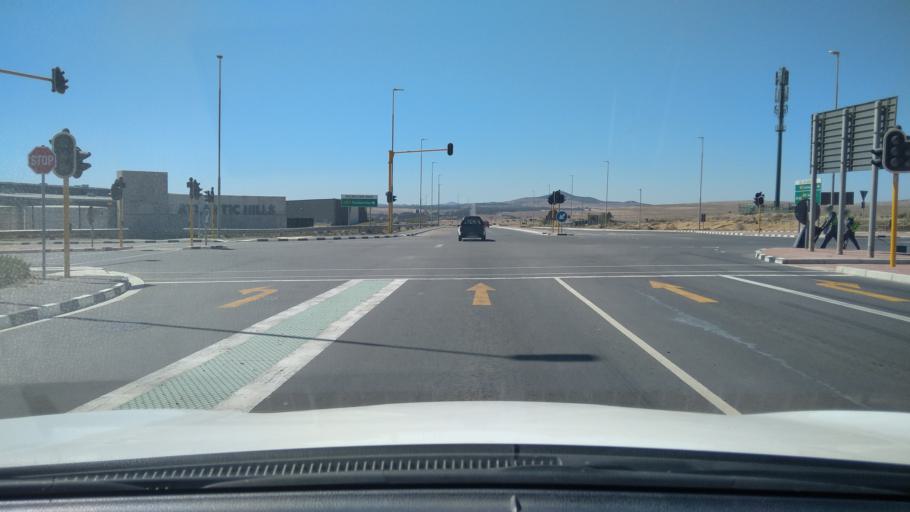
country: ZA
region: Western Cape
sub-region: City of Cape Town
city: Sunset Beach
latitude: -33.8185
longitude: 18.5520
